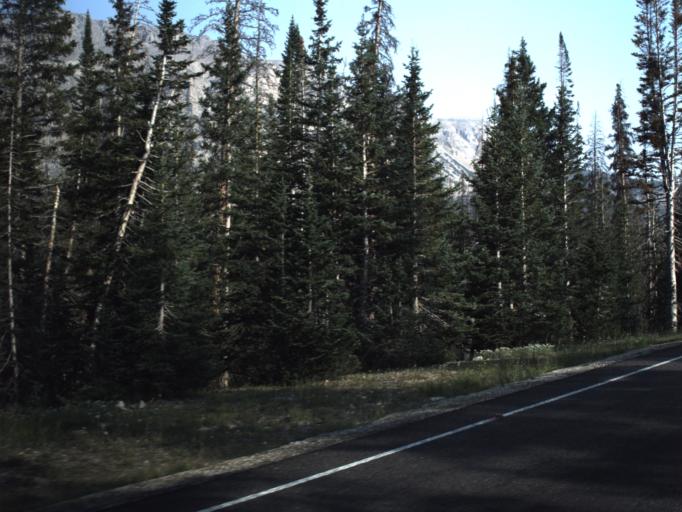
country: US
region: Utah
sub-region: Summit County
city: Kamas
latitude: 40.7413
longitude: -110.8709
